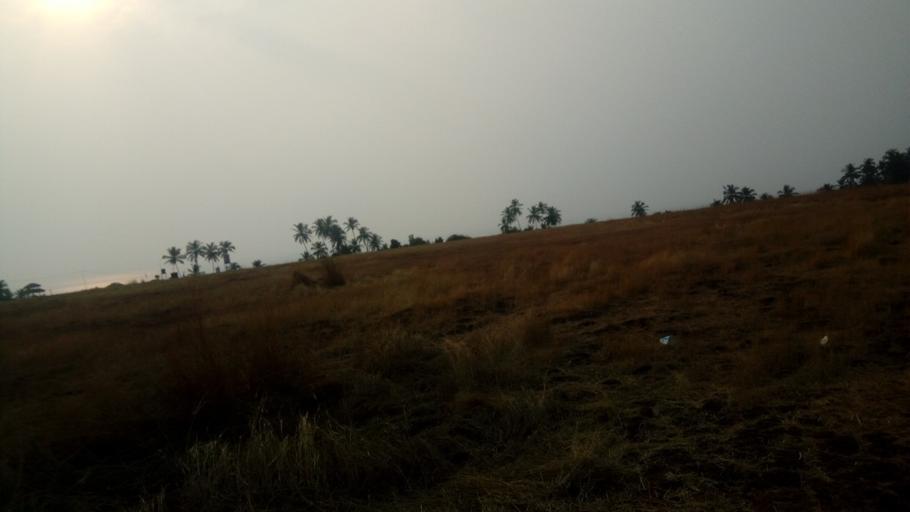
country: IN
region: Goa
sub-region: South Goa
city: Cavelossim
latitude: 15.0997
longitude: 73.9289
